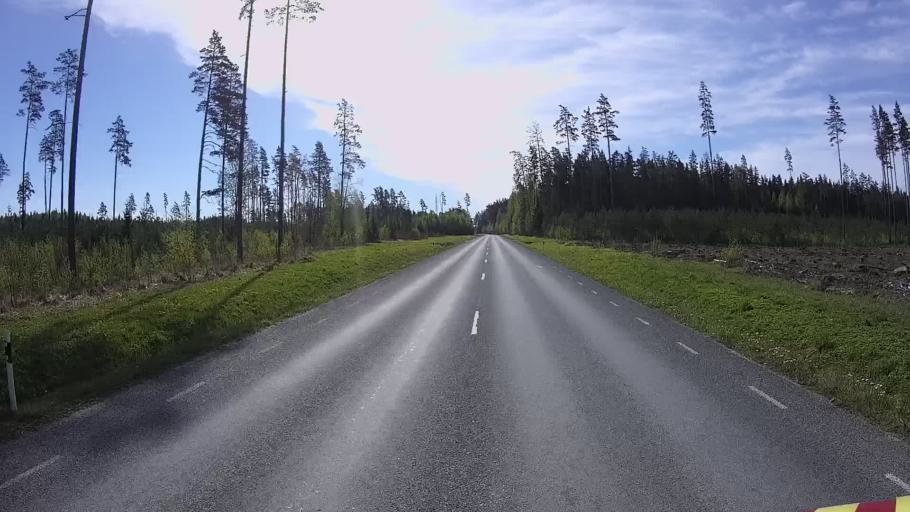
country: EE
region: Polvamaa
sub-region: Polva linn
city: Polva
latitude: 58.1666
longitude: 27.1464
